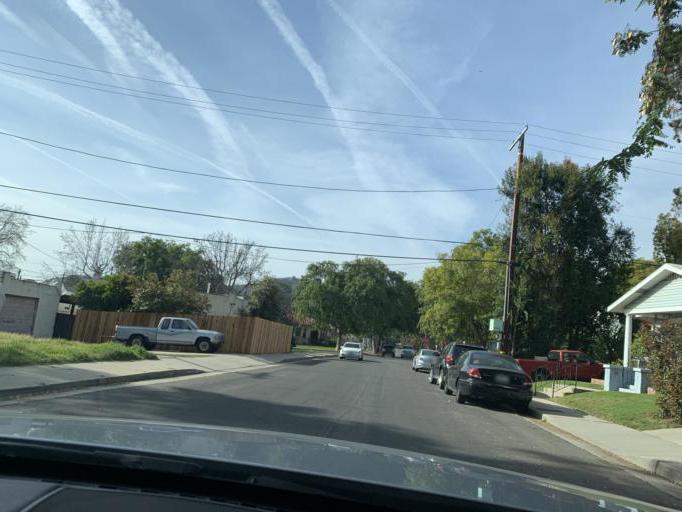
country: US
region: California
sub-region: Los Angeles County
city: Pasadena
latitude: 34.1418
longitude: -118.1920
